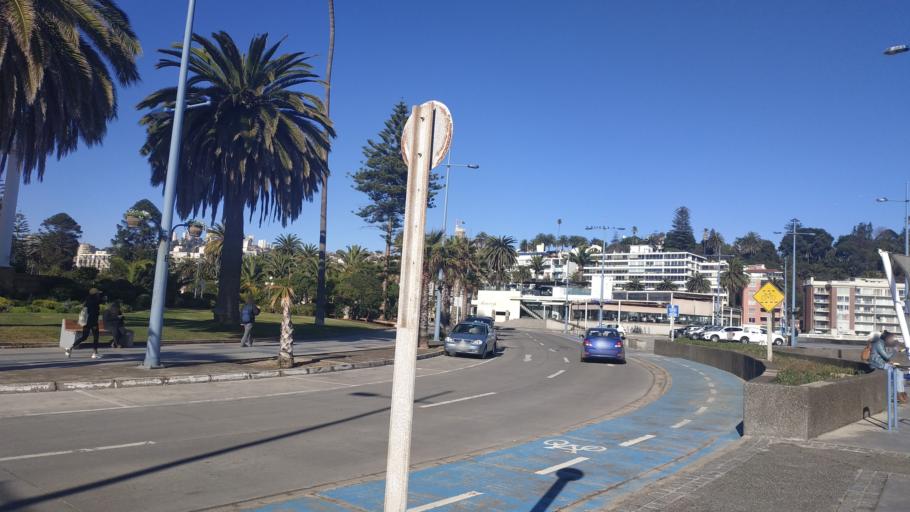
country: CL
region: Valparaiso
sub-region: Provincia de Valparaiso
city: Vina del Mar
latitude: -33.0182
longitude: -71.5613
